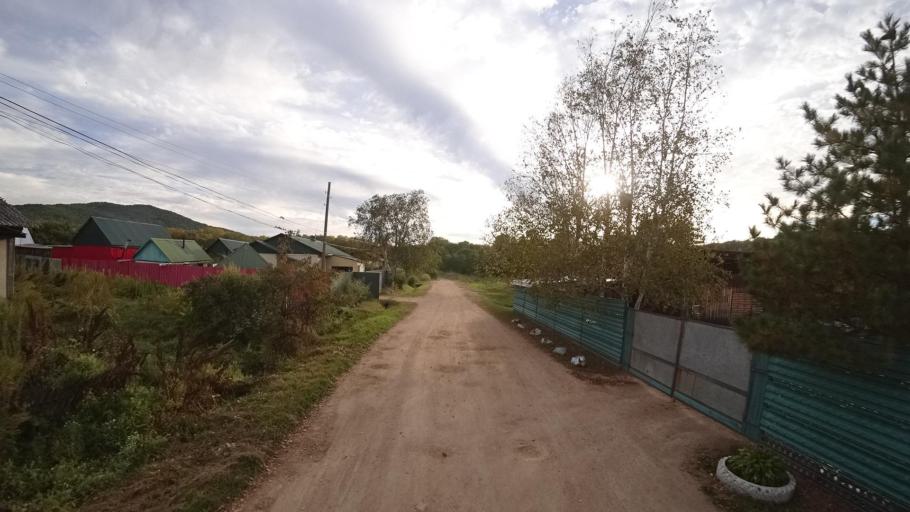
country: RU
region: Primorskiy
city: Yakovlevka
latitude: 44.4194
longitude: 133.4482
